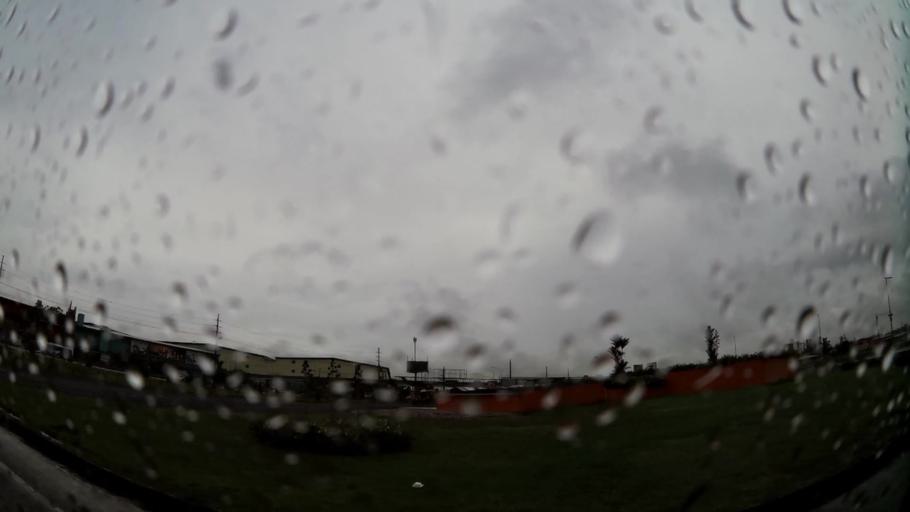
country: PA
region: Colon
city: Arco Iris
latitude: 9.3369
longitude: -79.8816
